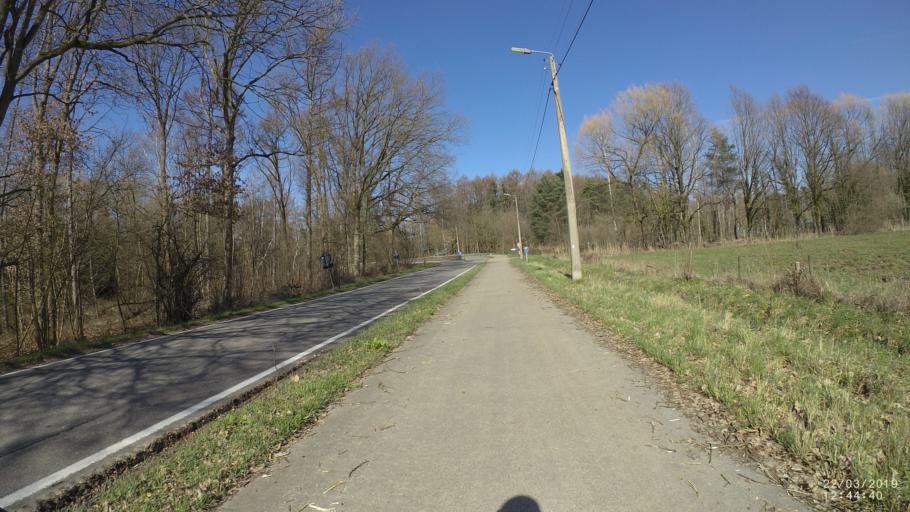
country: BE
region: Flanders
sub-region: Provincie Limburg
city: Zutendaal
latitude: 50.8910
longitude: 5.5642
